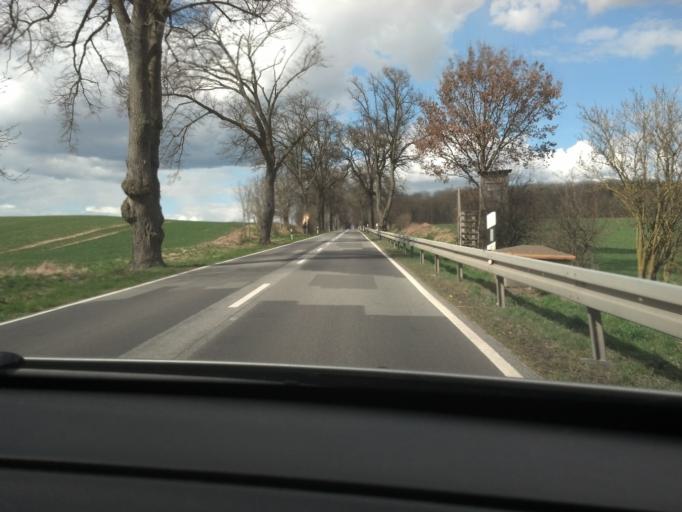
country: DE
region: Mecklenburg-Vorpommern
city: Burg Stargard
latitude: 53.4711
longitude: 13.3502
